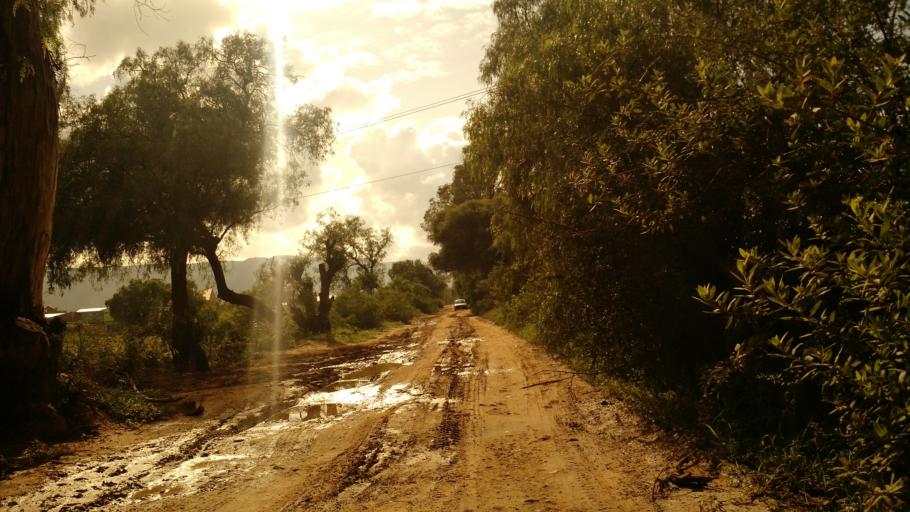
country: BO
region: Cochabamba
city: Cochabamba
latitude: -17.4545
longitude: -66.1494
